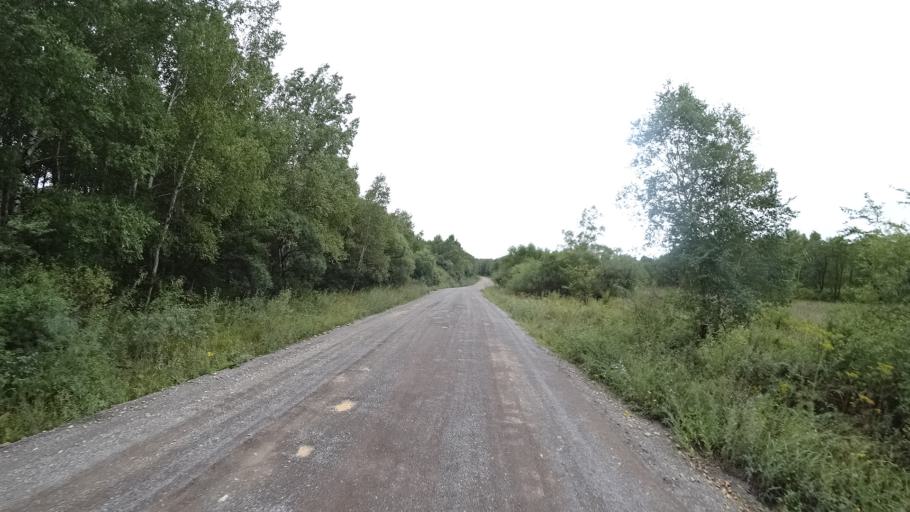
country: RU
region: Primorskiy
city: Ivanovka
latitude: 44.0425
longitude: 132.4946
